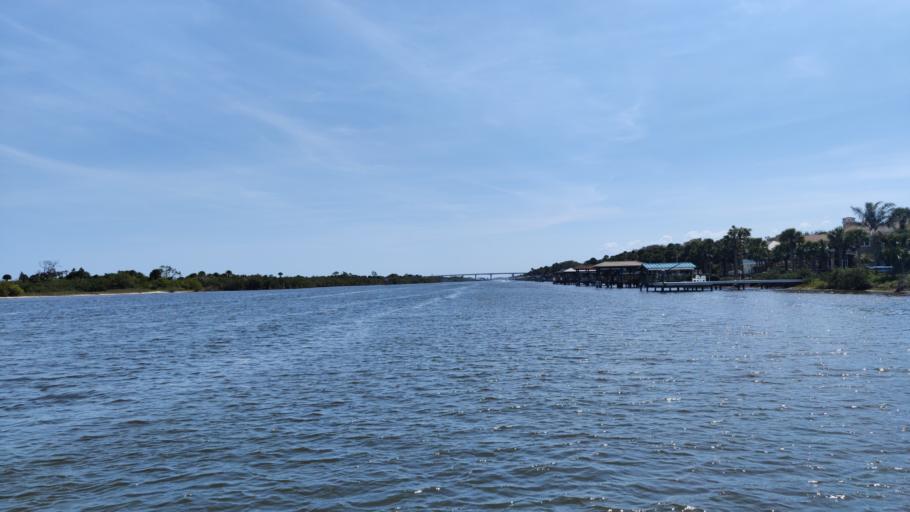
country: US
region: Florida
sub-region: Flagler County
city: Flagler Beach
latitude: 29.4954
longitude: -81.1431
